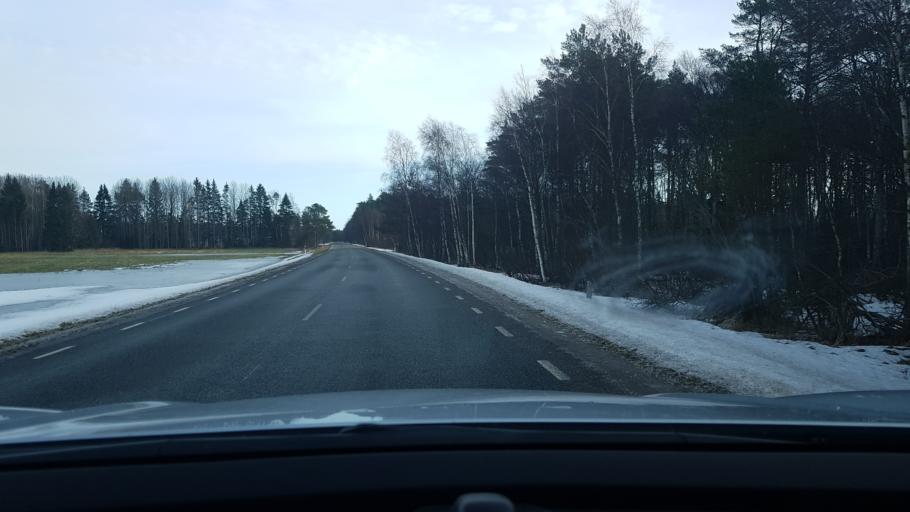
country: EE
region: Saare
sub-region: Kuressaare linn
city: Kuressaare
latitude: 58.4287
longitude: 22.6888
